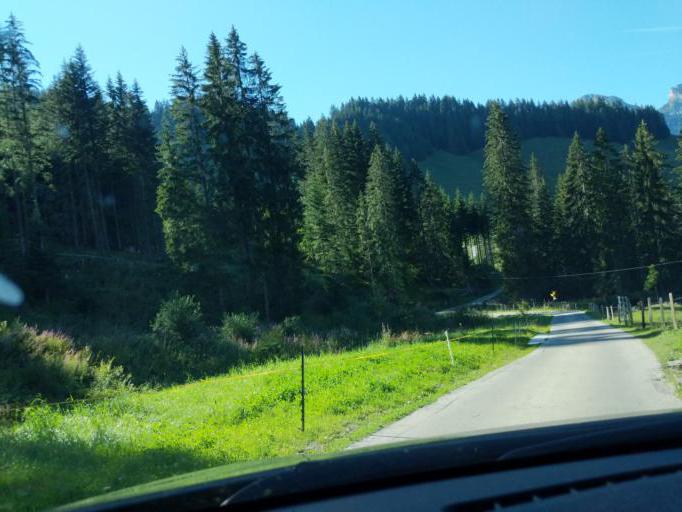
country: CH
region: Bern
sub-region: Obersimmental-Saanen District
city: Saanen
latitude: 46.5929
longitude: 7.2695
